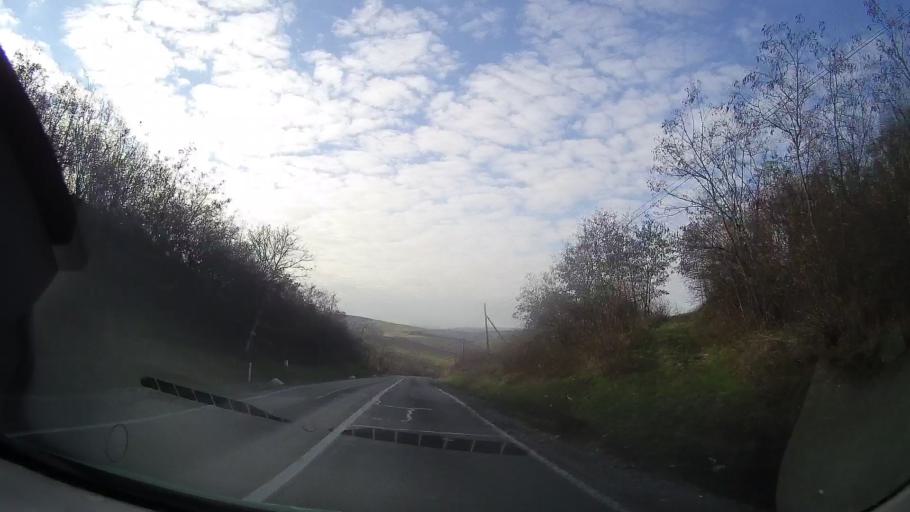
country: RO
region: Cluj
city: Jucu Herghelia
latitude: 46.8110
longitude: 23.8342
